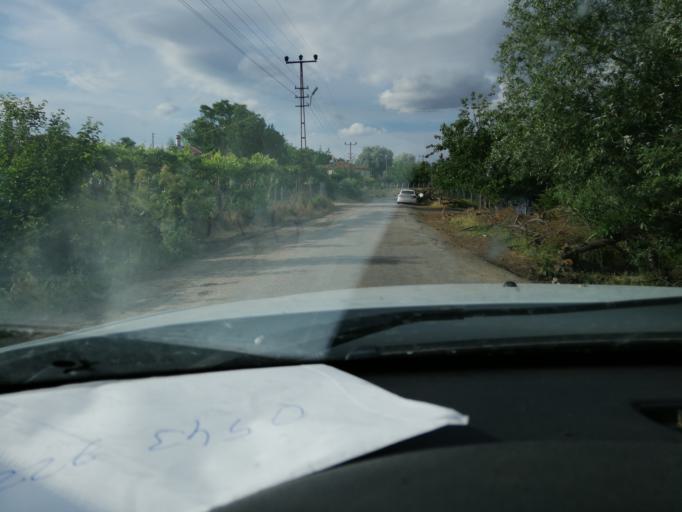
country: TR
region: Kirsehir
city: Kirsehir
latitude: 39.0250
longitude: 34.1249
